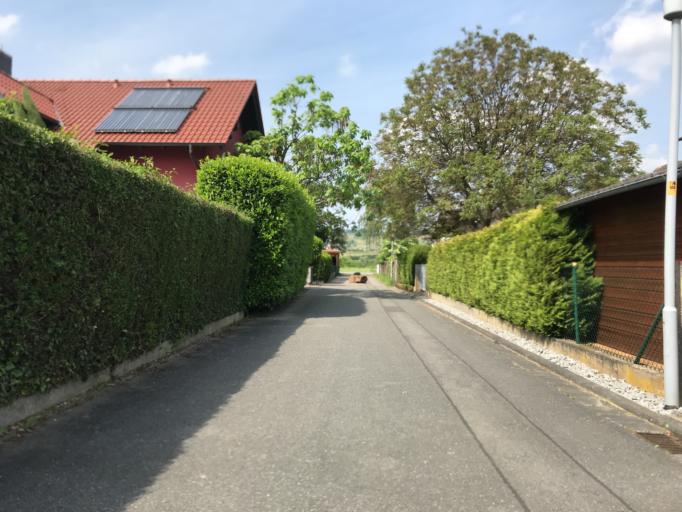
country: DE
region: Rheinland-Pfalz
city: Stadecken-Elsheim
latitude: 49.9087
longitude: 8.1278
